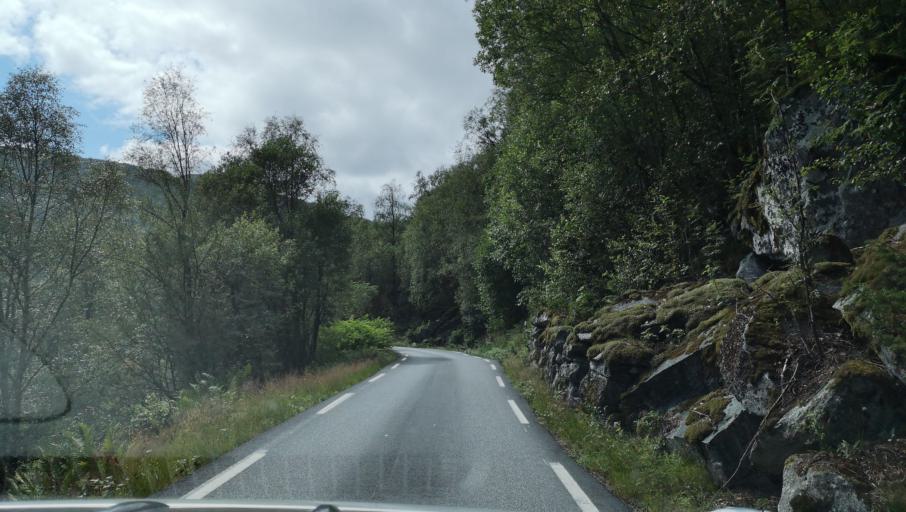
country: NO
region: Hordaland
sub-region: Modalen
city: Mo
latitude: 60.7856
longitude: 5.9269
